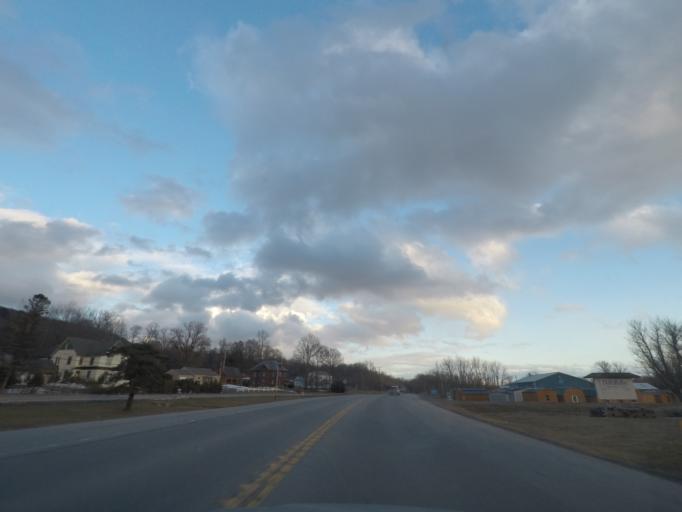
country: US
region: New York
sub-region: Montgomery County
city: Saint Johnsville
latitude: 42.9967
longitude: -74.6635
